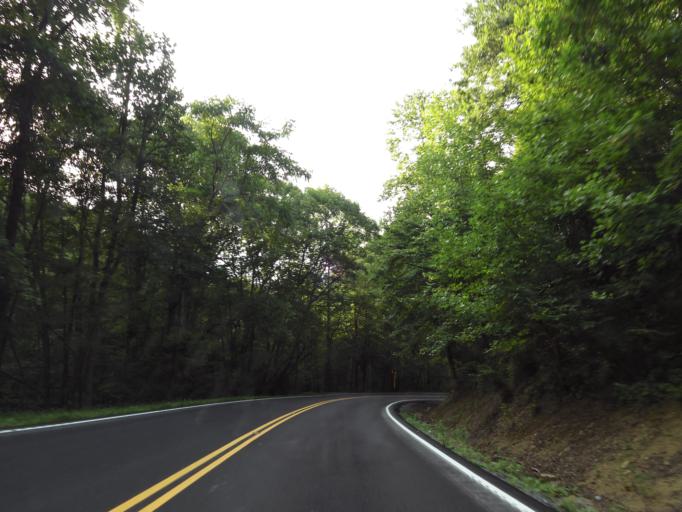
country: US
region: Tennessee
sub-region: Morgan County
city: Coalfield
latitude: 36.1221
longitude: -84.4305
